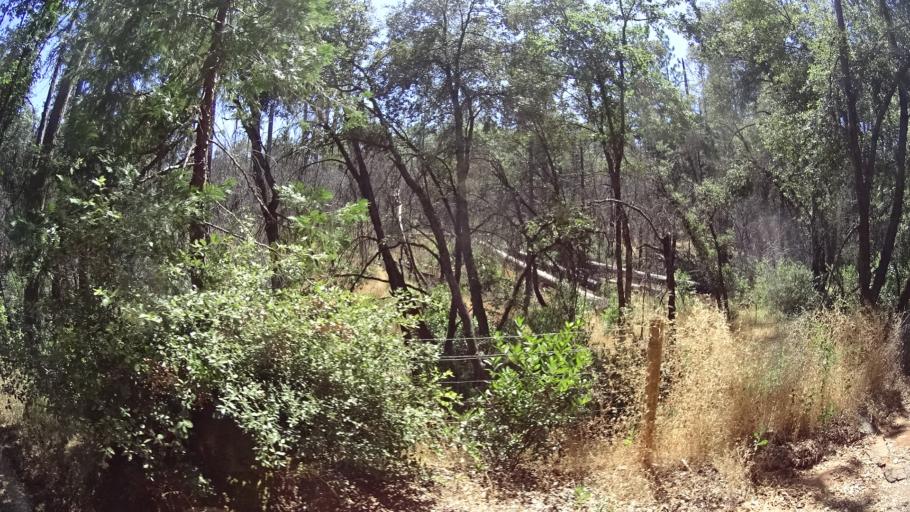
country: US
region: California
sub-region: Calaveras County
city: Mountain Ranch
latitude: 38.2853
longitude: -120.5836
